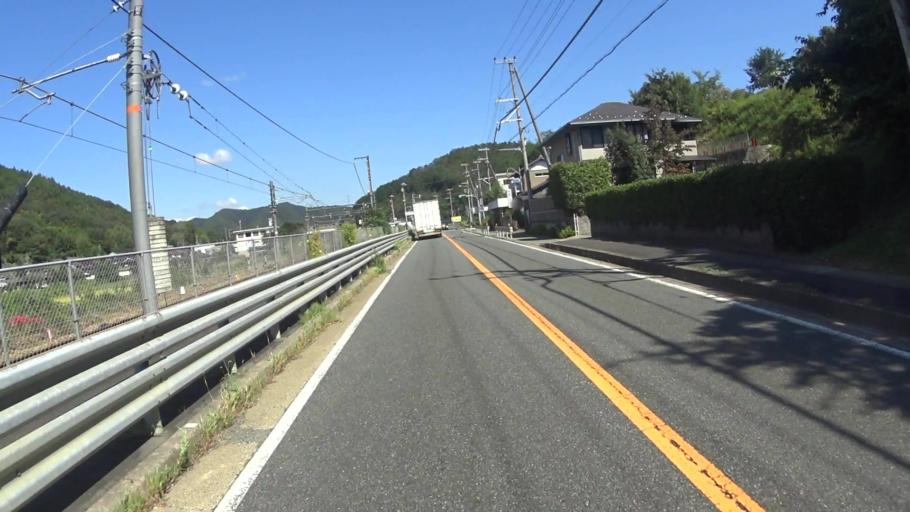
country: JP
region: Kyoto
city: Ayabe
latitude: 35.3461
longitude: 135.3117
